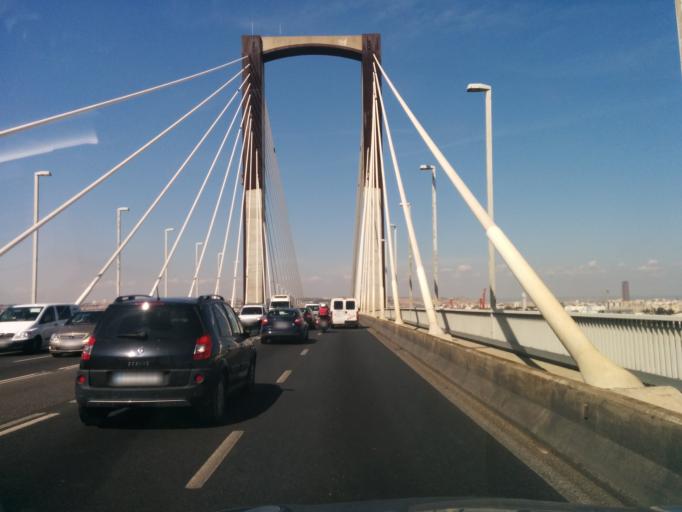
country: ES
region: Andalusia
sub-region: Provincia de Sevilla
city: Gelves
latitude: 37.3491
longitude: -5.9932
